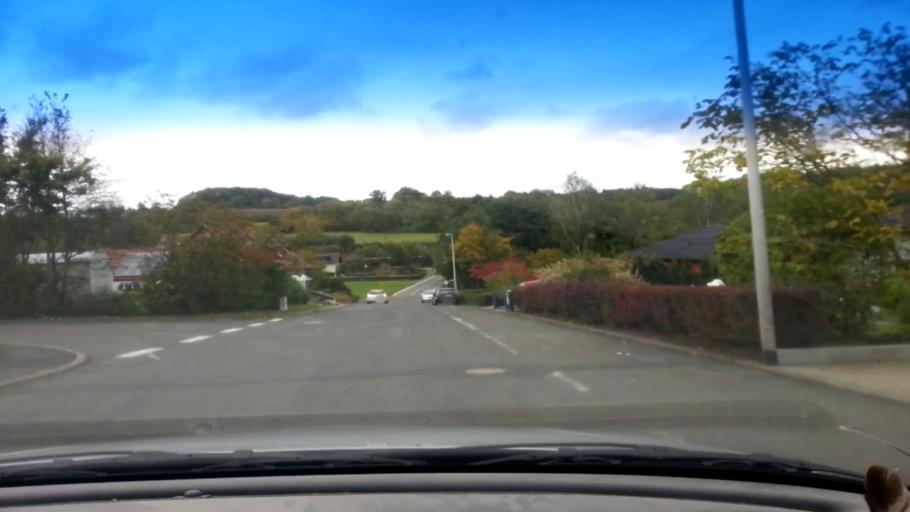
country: DE
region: Bavaria
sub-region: Upper Franconia
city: Gerach
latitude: 50.0317
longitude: 10.8108
